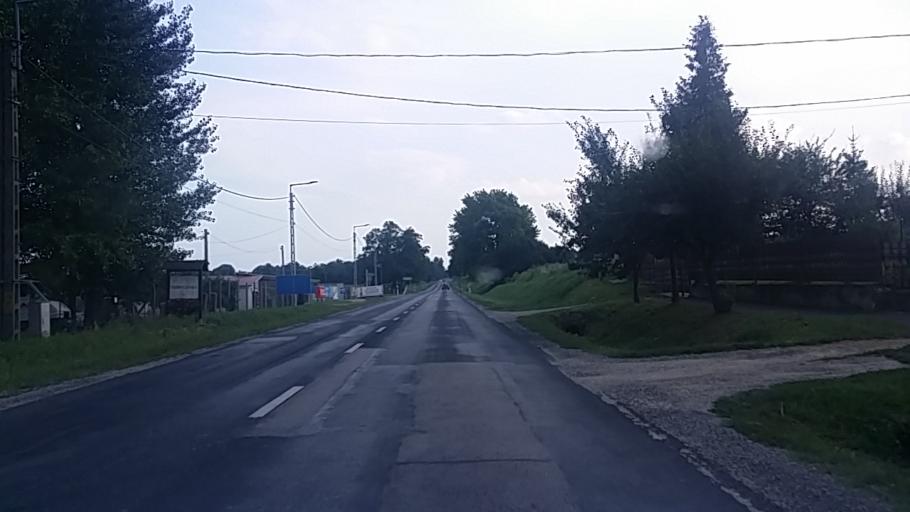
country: HU
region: Zala
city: Sarmellek
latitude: 46.7513
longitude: 17.1752
